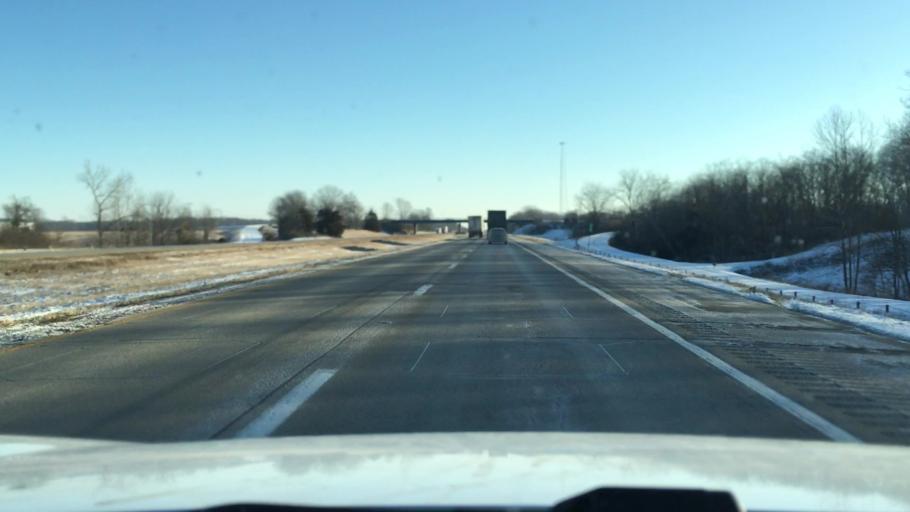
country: US
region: Illinois
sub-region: Effingham County
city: Effingham
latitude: 39.0833
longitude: -88.6189
